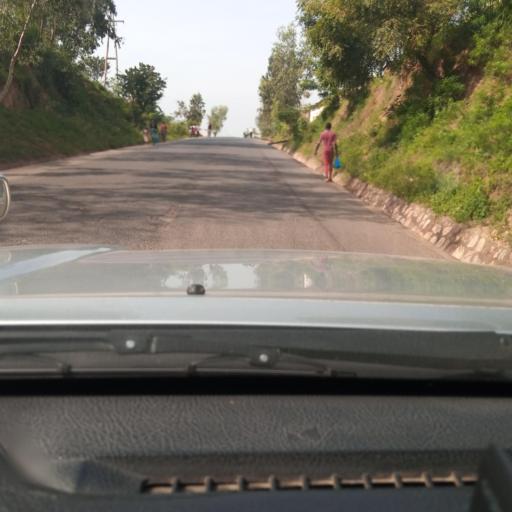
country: BI
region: Bujumbura Mairie
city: Bujumbura
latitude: -3.4823
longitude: 29.3532
